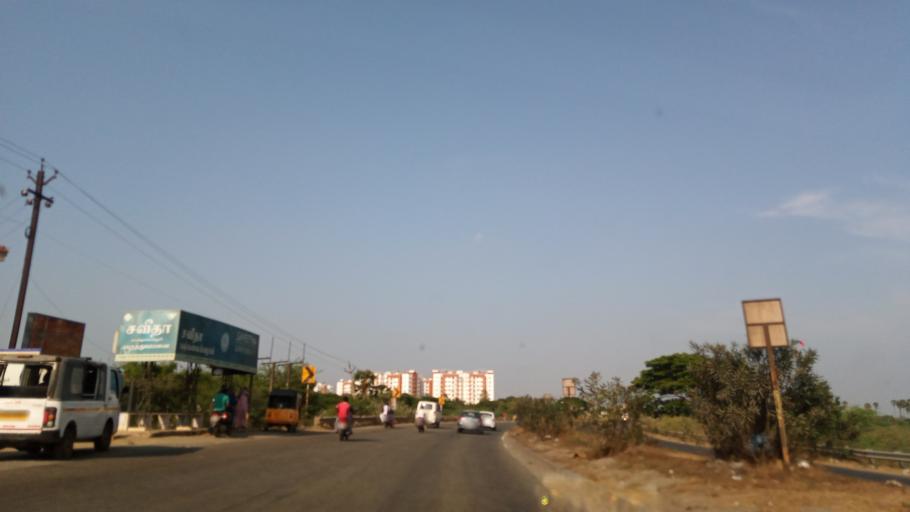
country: IN
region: Tamil Nadu
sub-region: Kancheepuram
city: Nandambakkam
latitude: 13.0222
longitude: 80.0167
